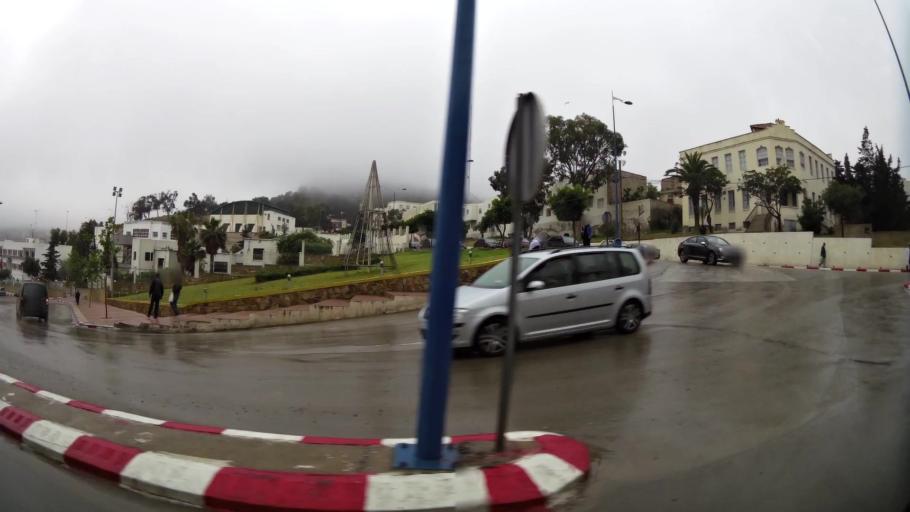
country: MA
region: Taza-Al Hoceima-Taounate
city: Al Hoceima
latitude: 35.2392
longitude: -3.9280
